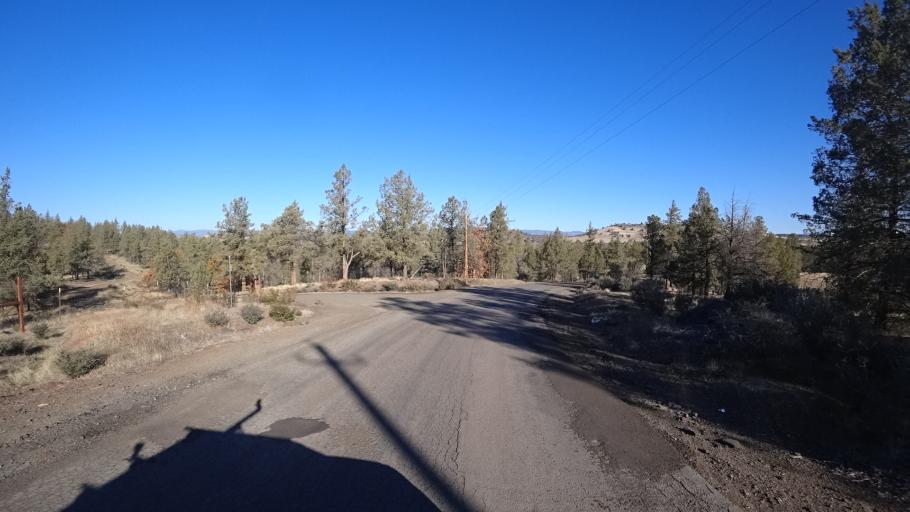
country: US
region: California
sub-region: Siskiyou County
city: Montague
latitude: 41.8842
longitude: -122.4458
